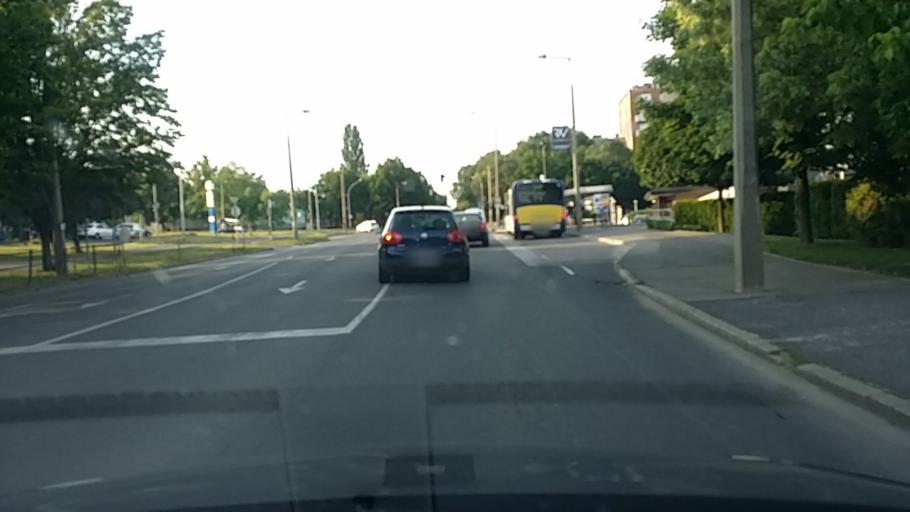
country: HU
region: Borsod-Abauj-Zemplen
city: Miskolc
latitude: 48.0828
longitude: 20.7853
